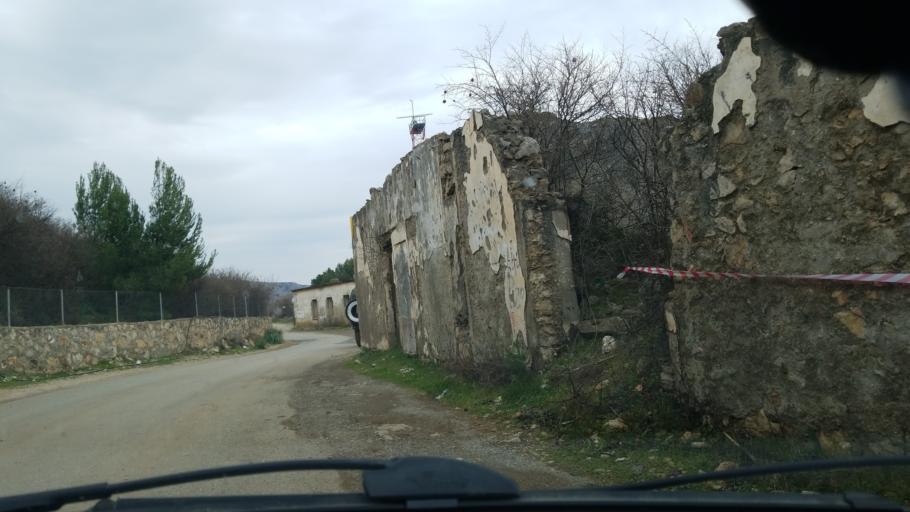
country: AL
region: Lezhe
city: Shengjin
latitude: 41.8111
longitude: 19.5819
